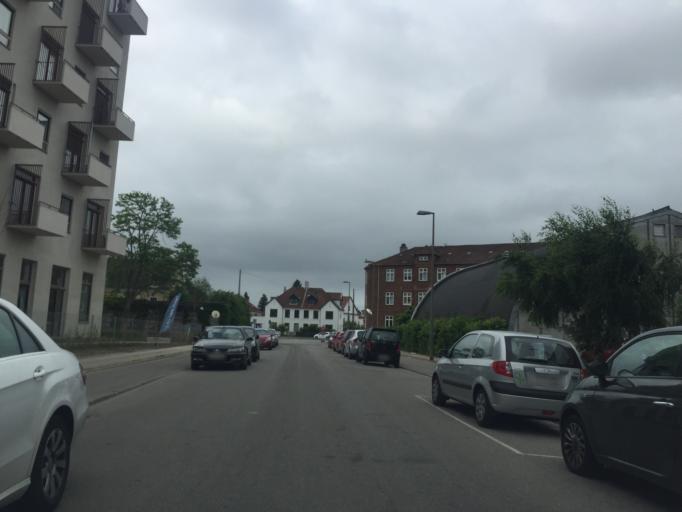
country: DK
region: Capital Region
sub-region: Kobenhavn
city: Vanlose
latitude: 55.6695
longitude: 12.4963
